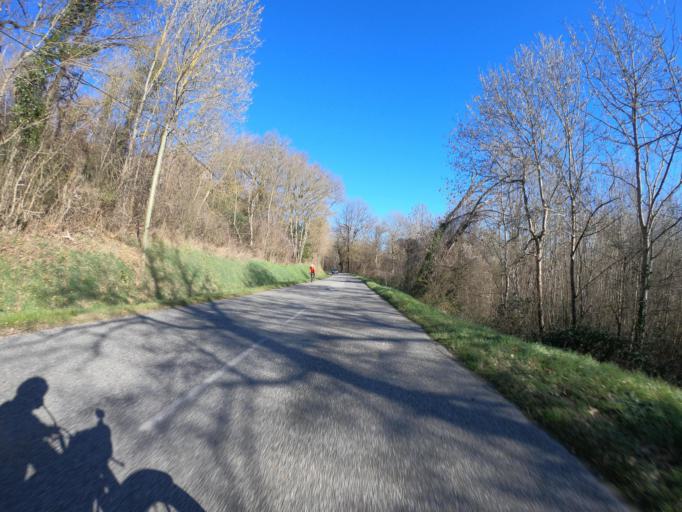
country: FR
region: Midi-Pyrenees
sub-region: Departement de l'Ariege
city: Mirepoix
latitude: 43.0845
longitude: 1.8258
